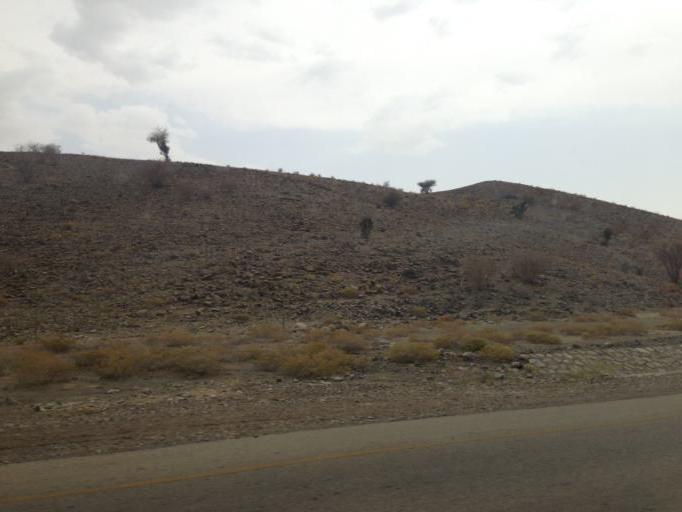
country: OM
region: Ash Sharqiyah
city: Badiyah
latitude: 22.5565
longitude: 59.0104
